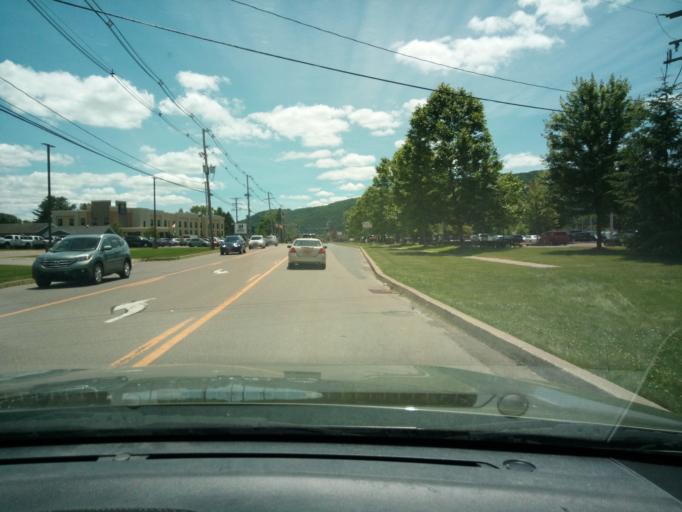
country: US
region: Pennsylvania
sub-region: Bradford County
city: South Waverly
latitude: 41.9811
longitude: -76.5429
